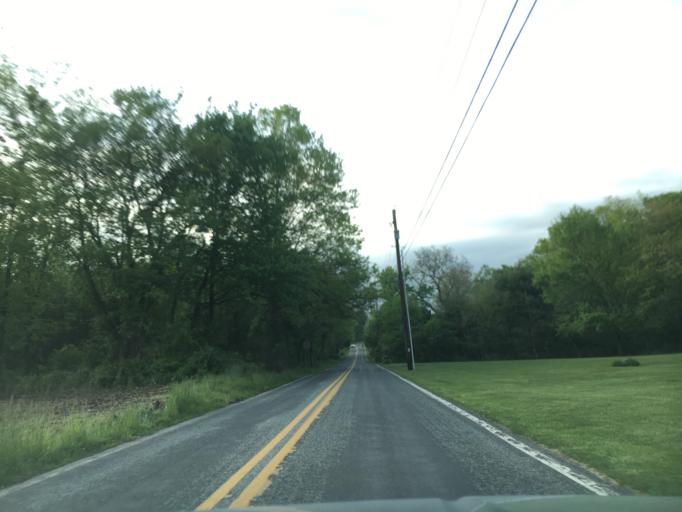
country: US
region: Pennsylvania
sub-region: Berks County
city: Fleetwood
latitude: 40.4485
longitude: -75.7802
